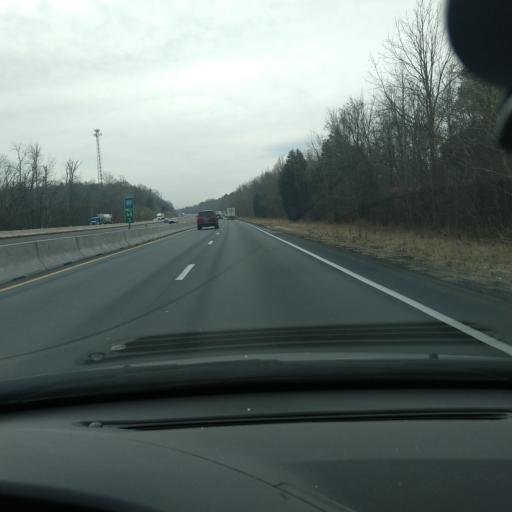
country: US
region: North Carolina
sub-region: Rowan County
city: Landis
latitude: 35.5248
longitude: -80.5724
